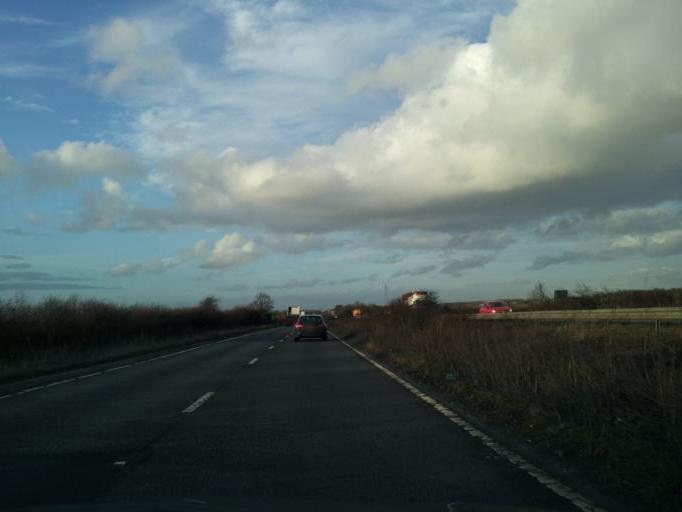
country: GB
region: England
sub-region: District of Rutland
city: Greetham
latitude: 52.7698
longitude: -0.6114
